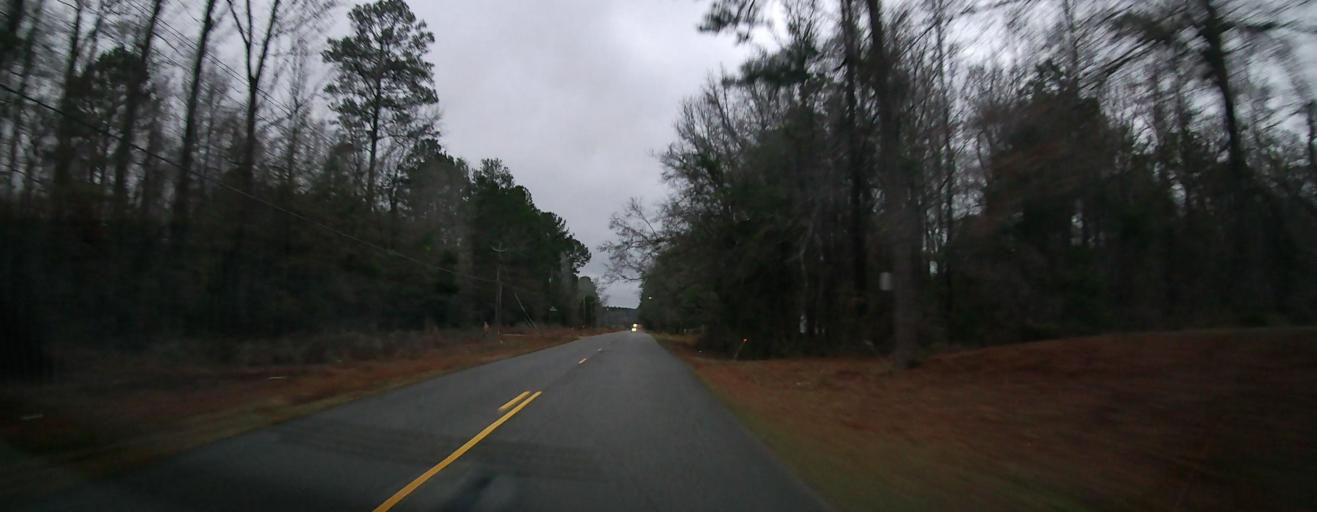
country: US
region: Alabama
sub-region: Tuscaloosa County
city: Vance
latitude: 33.1487
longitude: -87.2298
